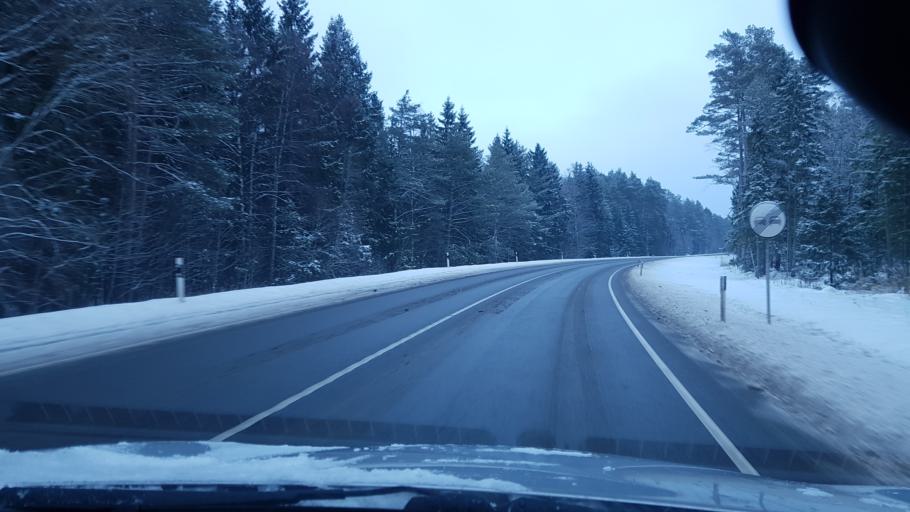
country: EE
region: Harju
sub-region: Keila linn
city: Keila
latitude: 59.3390
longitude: 24.2539
